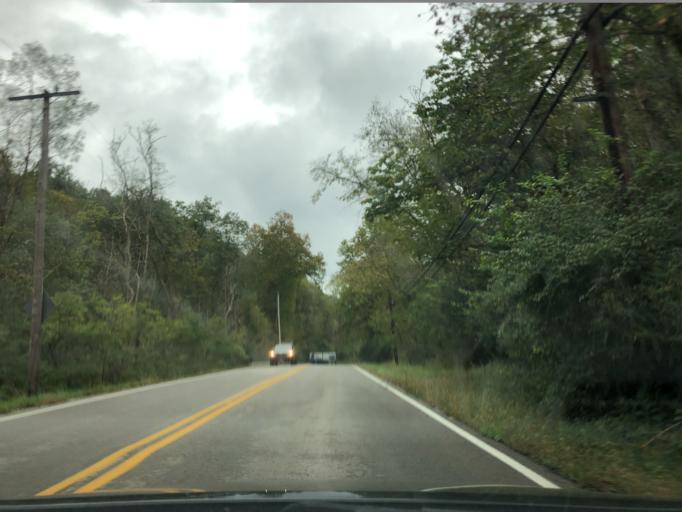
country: US
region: Ohio
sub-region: Hamilton County
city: Mariemont
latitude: 39.1672
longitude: -84.3780
